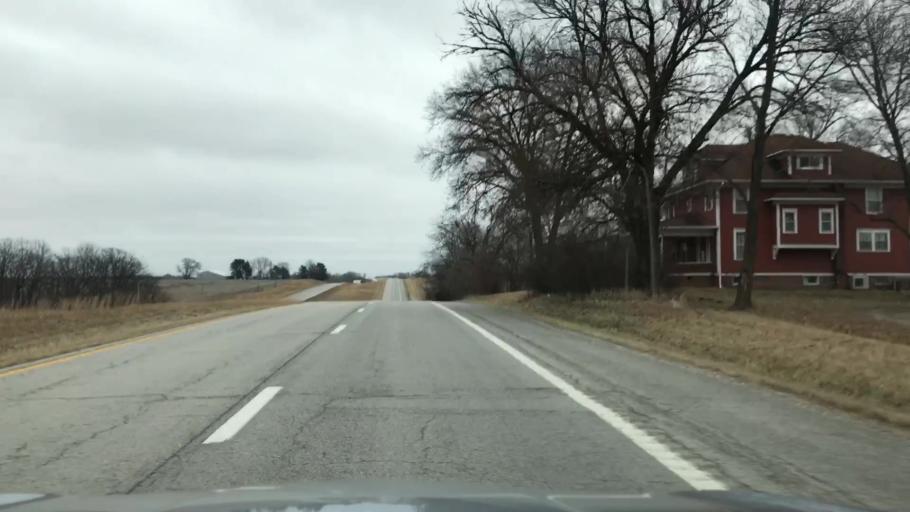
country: US
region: Missouri
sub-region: Linn County
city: Brookfield
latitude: 39.7785
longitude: -93.1641
